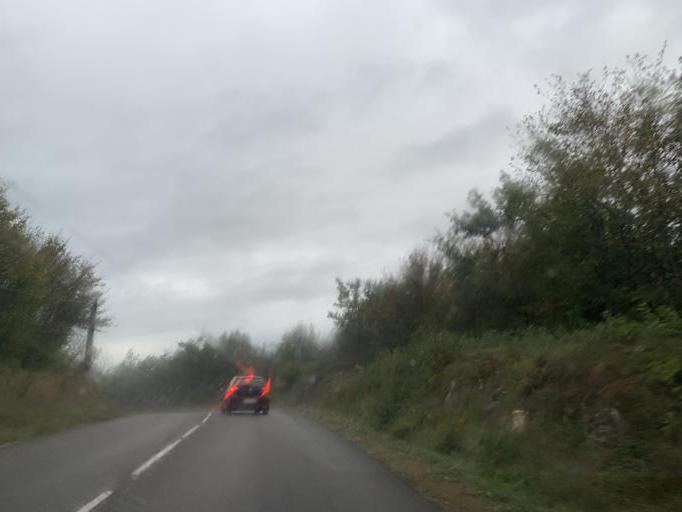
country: FR
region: Rhone-Alpes
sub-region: Departement de l'Ain
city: Belley
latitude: 45.7012
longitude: 5.6504
